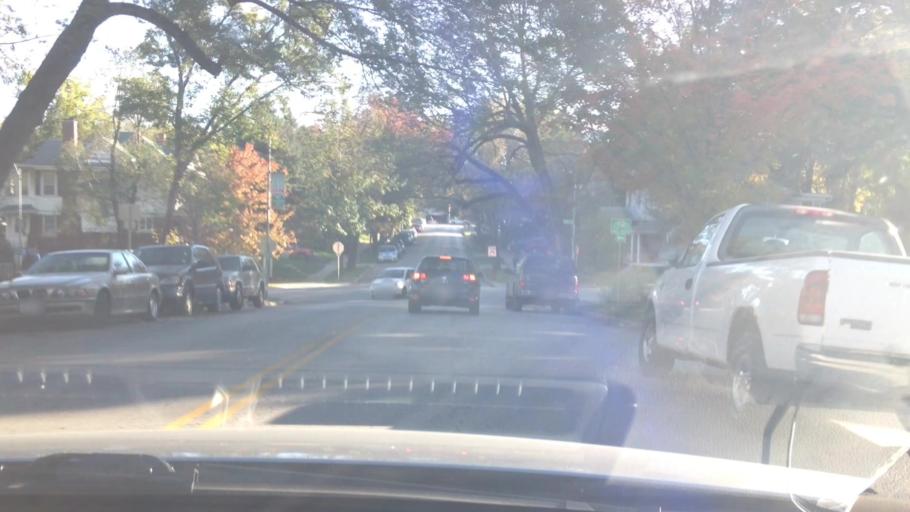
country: US
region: Kansas
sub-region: Johnson County
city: Westwood
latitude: 39.0591
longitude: -94.6037
